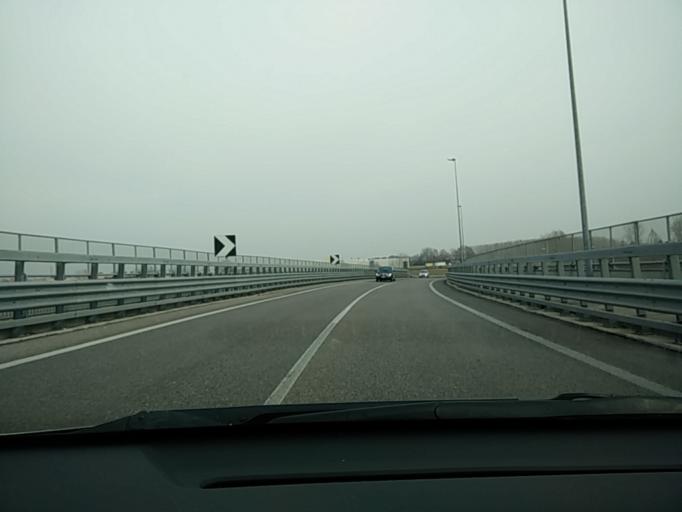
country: IT
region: Veneto
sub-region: Provincia di Venezia
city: San Dona di Piave
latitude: 45.6347
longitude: 12.5996
